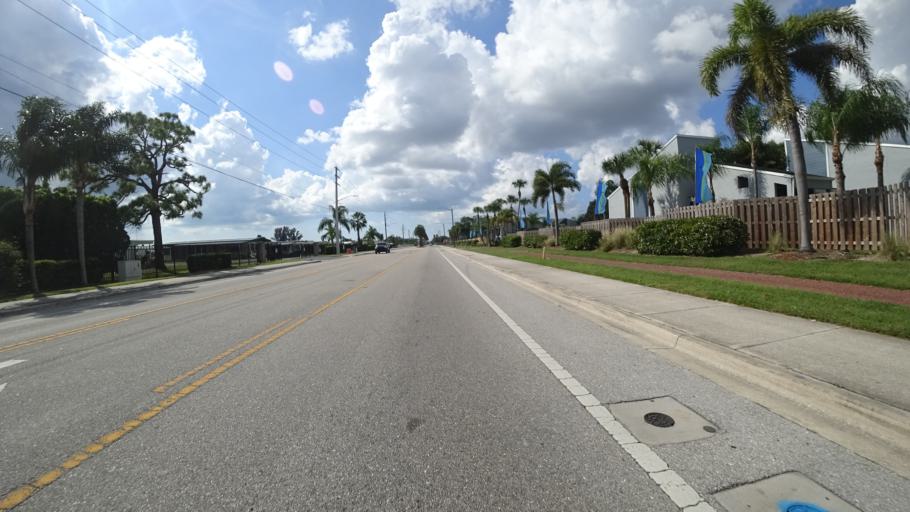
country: US
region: Florida
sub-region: Manatee County
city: South Bradenton
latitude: 27.4404
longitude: -82.5689
